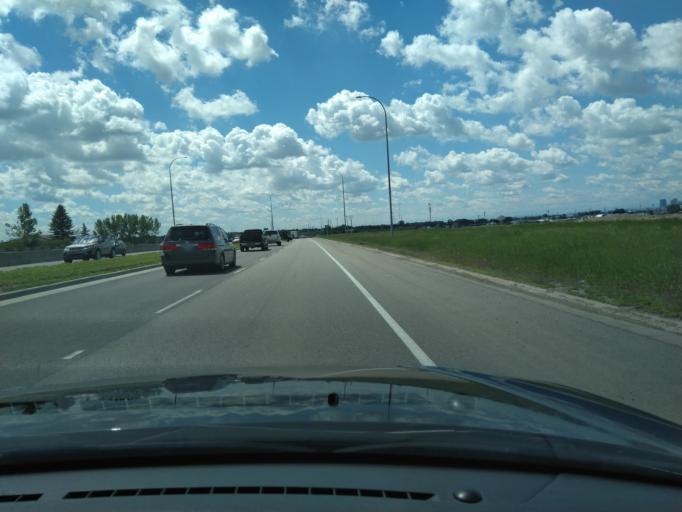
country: CA
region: Alberta
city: Calgary
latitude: 51.1299
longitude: -113.9703
